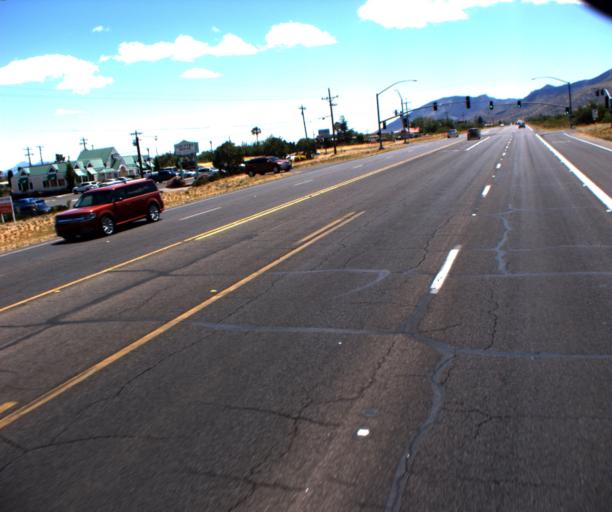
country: US
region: Arizona
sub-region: Cochise County
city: Sierra Vista Southeast
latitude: 31.4902
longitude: -110.2575
